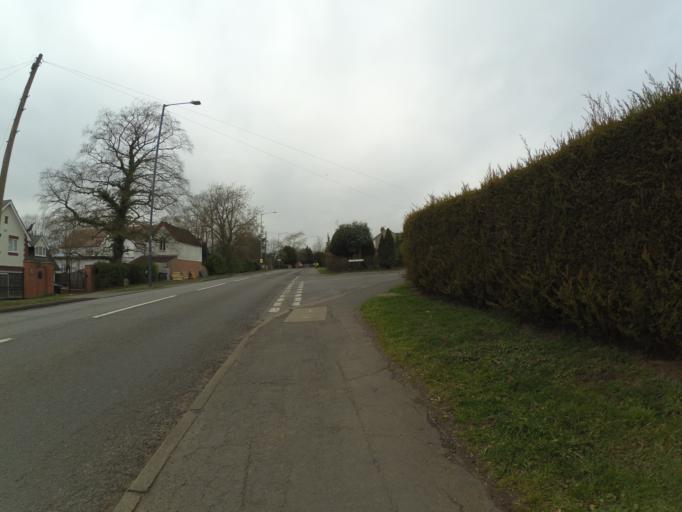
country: GB
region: England
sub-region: Warwickshire
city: Rugby
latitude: 52.3566
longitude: -1.2049
